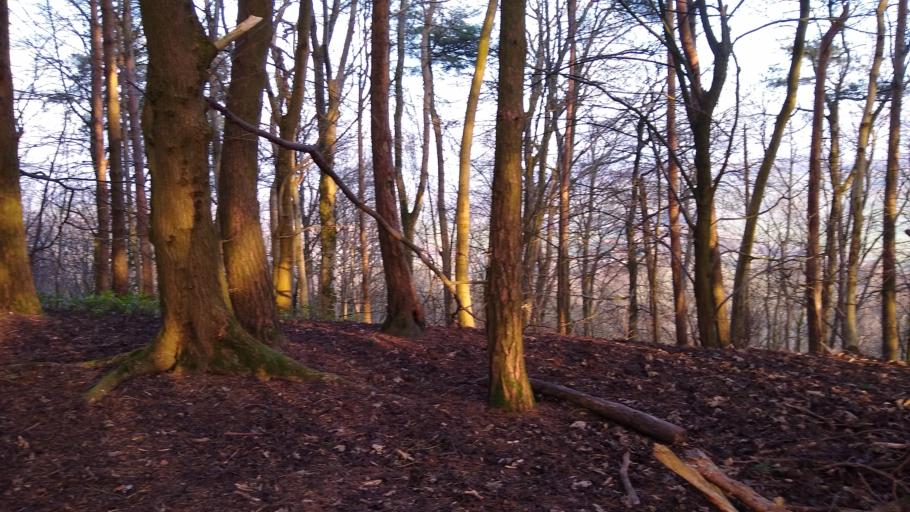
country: GB
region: England
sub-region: Cumbria
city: Penrith
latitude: 54.6140
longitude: -2.8255
